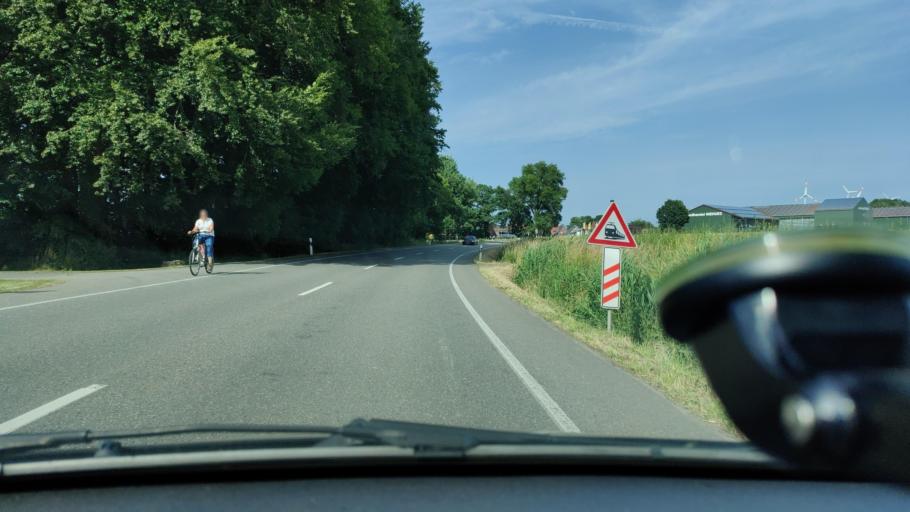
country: DE
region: North Rhine-Westphalia
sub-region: Regierungsbezirk Munster
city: Legden
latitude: 51.9964
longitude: 7.1198
